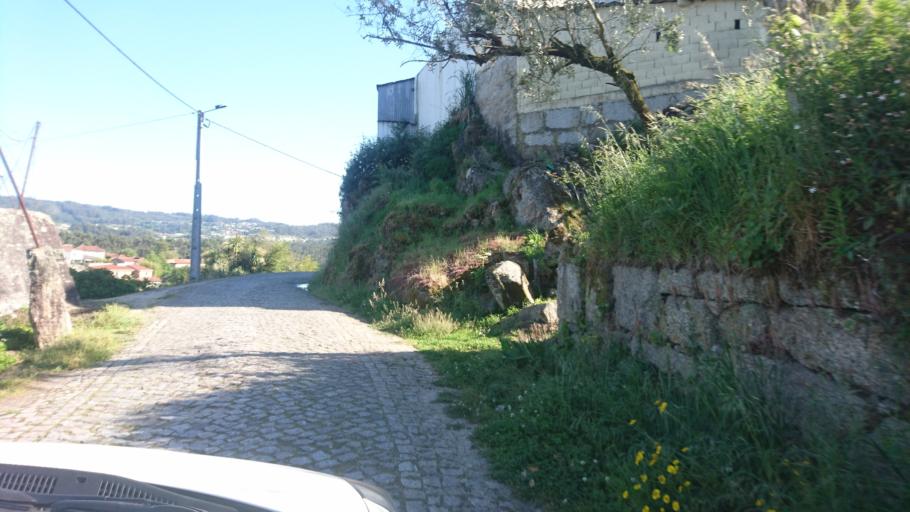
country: PT
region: Porto
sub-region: Paredes
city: Baltar
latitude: 41.1662
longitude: -8.3750
